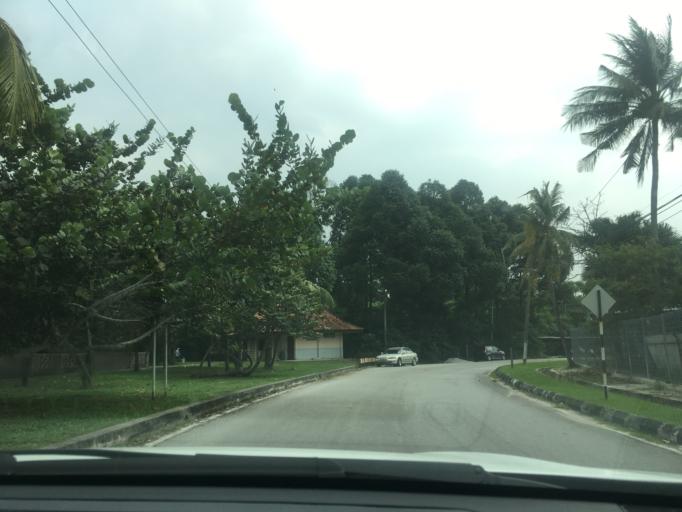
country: MY
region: Selangor
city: Klang
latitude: 3.0487
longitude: 101.4408
